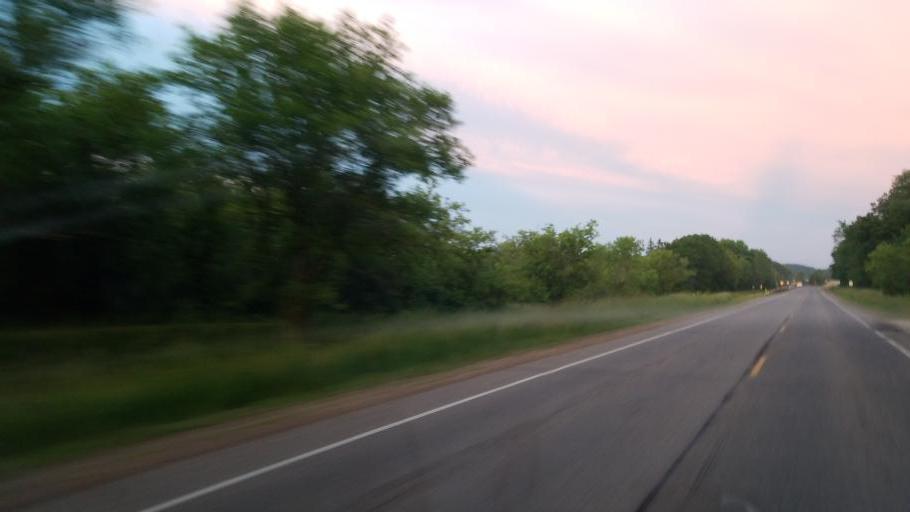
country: US
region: Wisconsin
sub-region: Juneau County
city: Elroy
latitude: 43.7464
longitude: -90.2788
